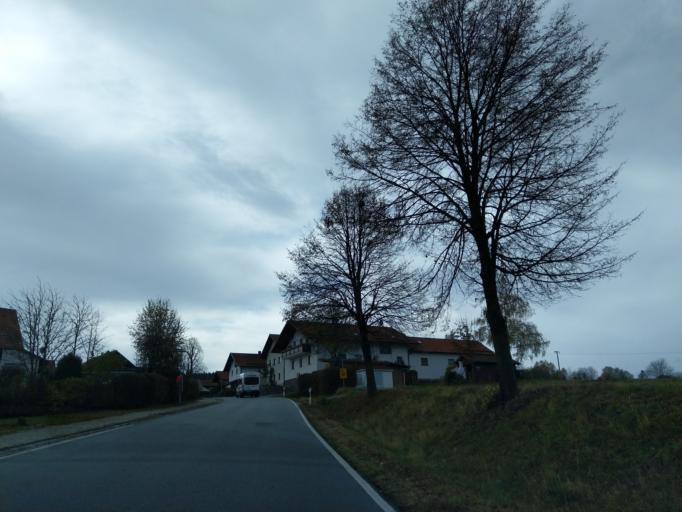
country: DE
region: Bavaria
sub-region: Lower Bavaria
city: Schofweg
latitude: 48.8425
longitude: 13.2277
